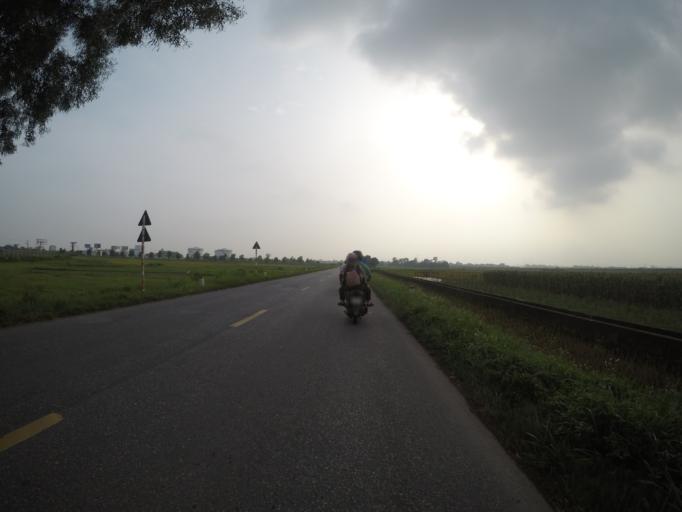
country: VN
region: Ha Noi
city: Me Linh
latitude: 21.2250
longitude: 105.7791
